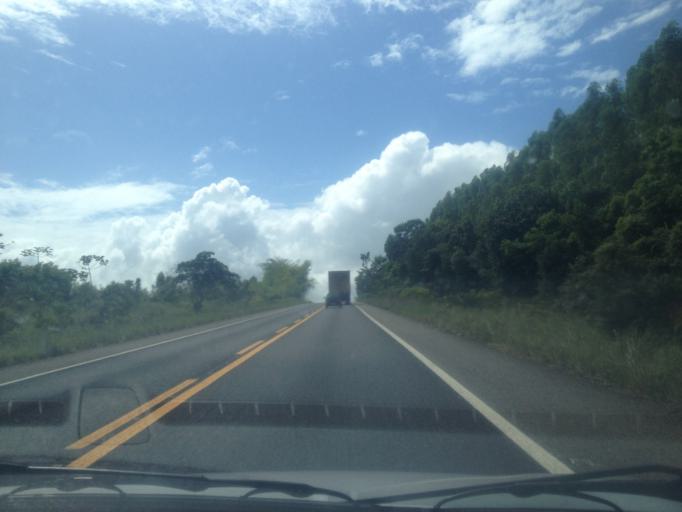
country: BR
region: Sergipe
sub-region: Indiaroba
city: Indiaroba
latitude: -11.6481
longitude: -37.5433
